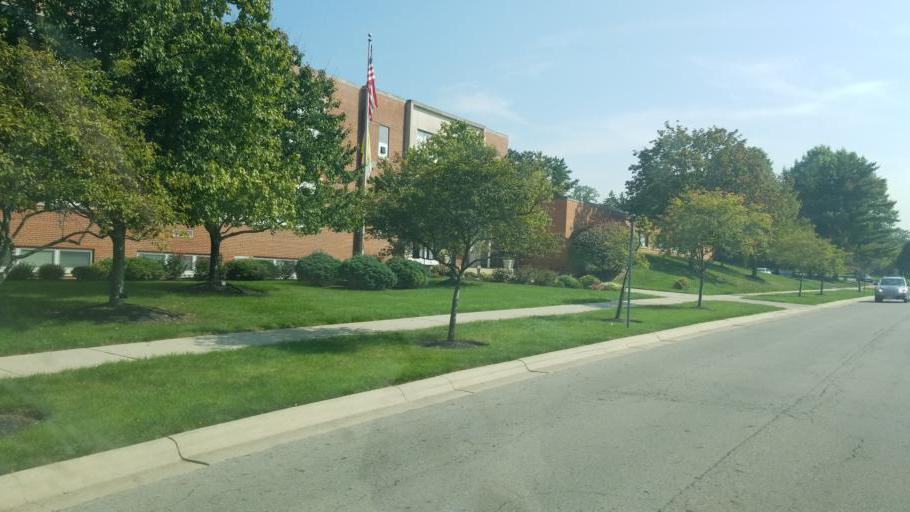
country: US
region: Ohio
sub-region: Franklin County
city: Worthington
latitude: 40.0772
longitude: -83.0174
